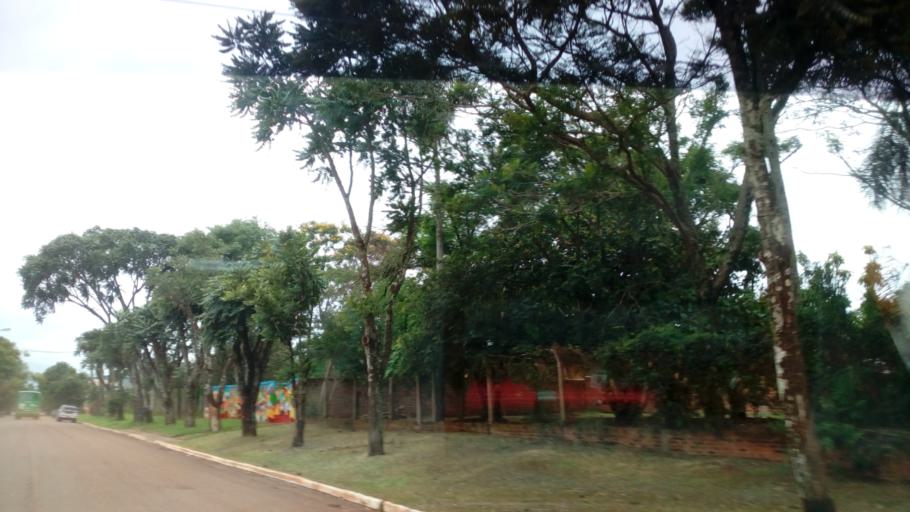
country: AR
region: Misiones
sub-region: Departamento de Candelaria
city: Candelaria
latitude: -27.4602
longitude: -55.7484
